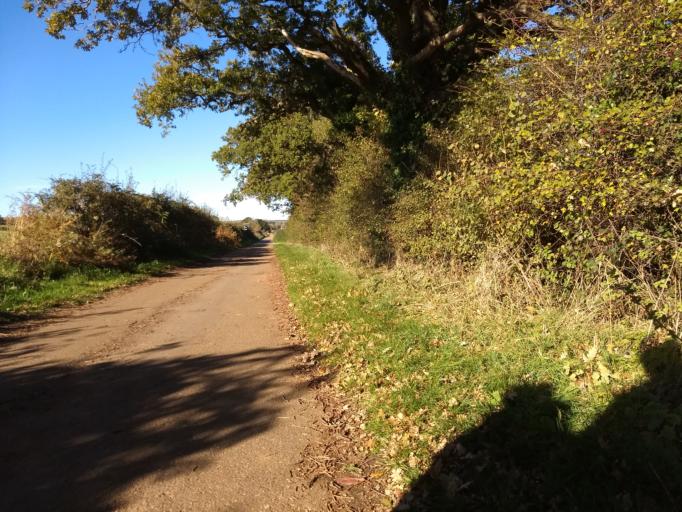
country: GB
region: England
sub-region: Isle of Wight
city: Newport
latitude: 50.6680
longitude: -1.2804
